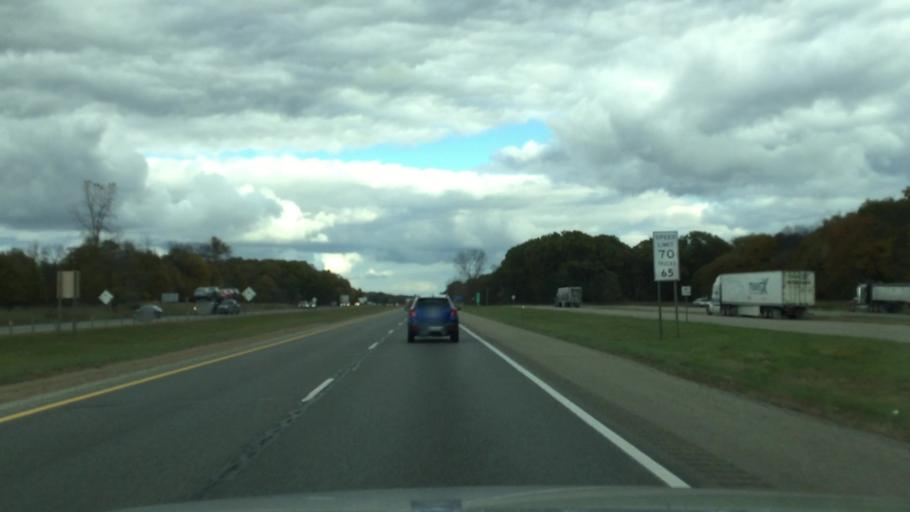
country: US
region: Michigan
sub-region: Kalamazoo County
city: Westwood
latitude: 42.2376
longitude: -85.6639
